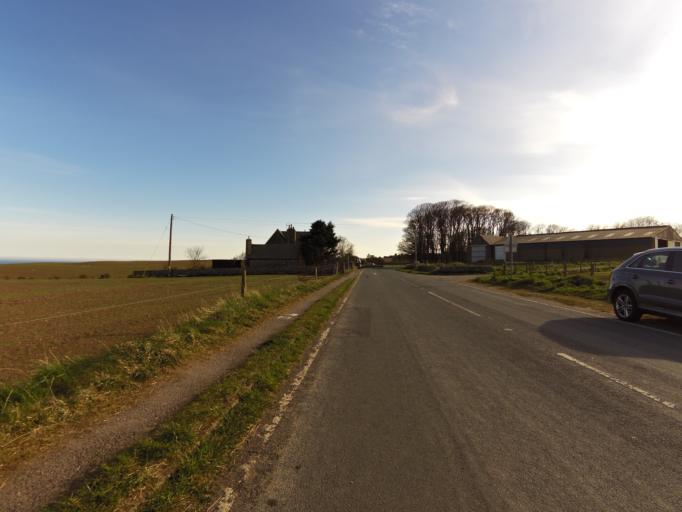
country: GB
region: Scotland
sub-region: Aberdeenshire
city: Stonehaven
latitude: 56.9462
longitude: -2.2057
